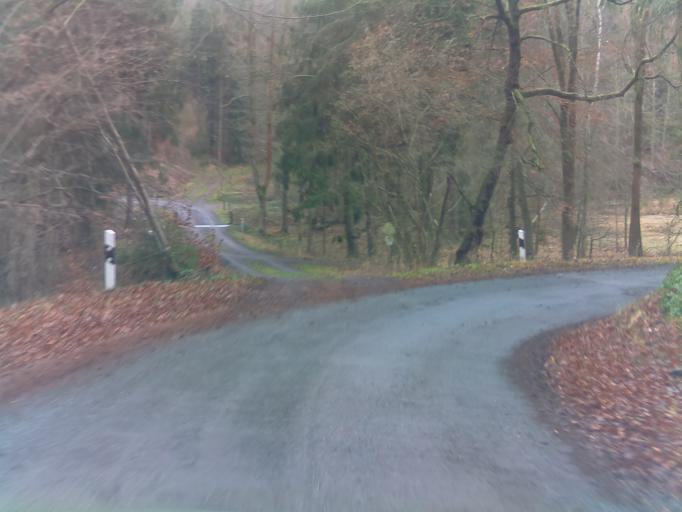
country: DE
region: Thuringia
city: Herschdorf
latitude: 50.7094
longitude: 11.4918
